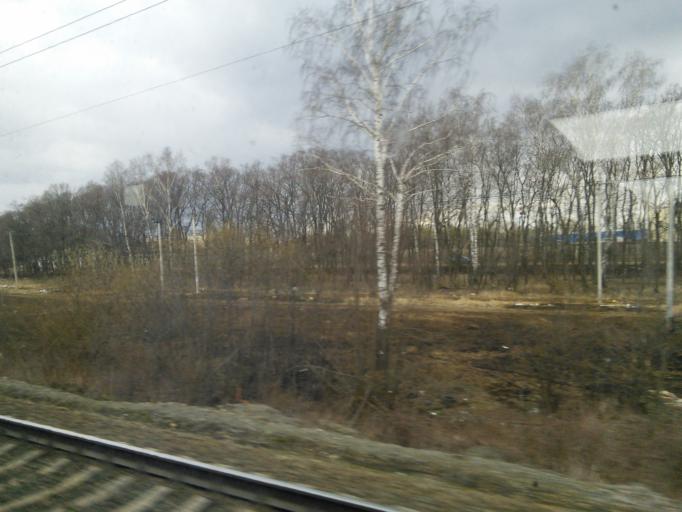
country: RU
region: Moskovskaya
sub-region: Podol'skiy Rayon
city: Podol'sk
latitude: 55.3985
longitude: 37.5443
